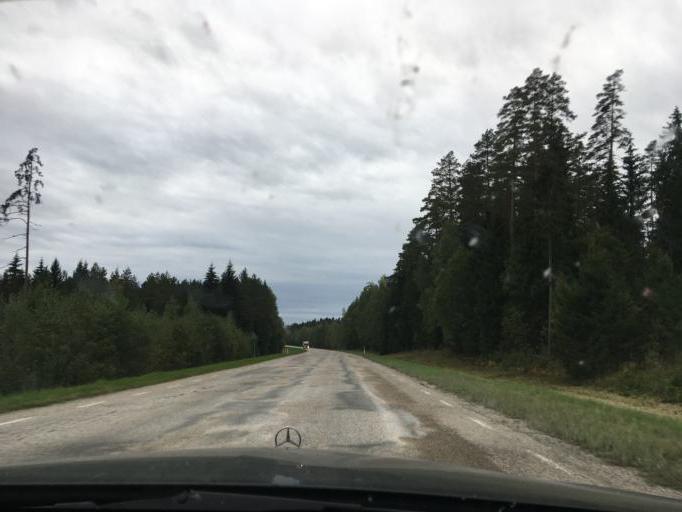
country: LV
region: Aluksnes Rajons
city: Aluksne
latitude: 57.6004
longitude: 27.1504
